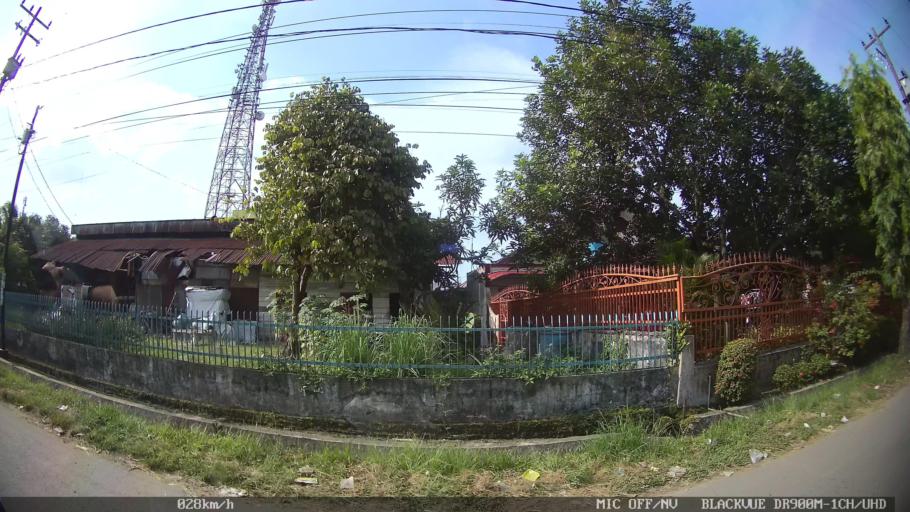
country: ID
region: North Sumatra
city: Binjai
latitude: 3.6108
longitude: 98.4963
